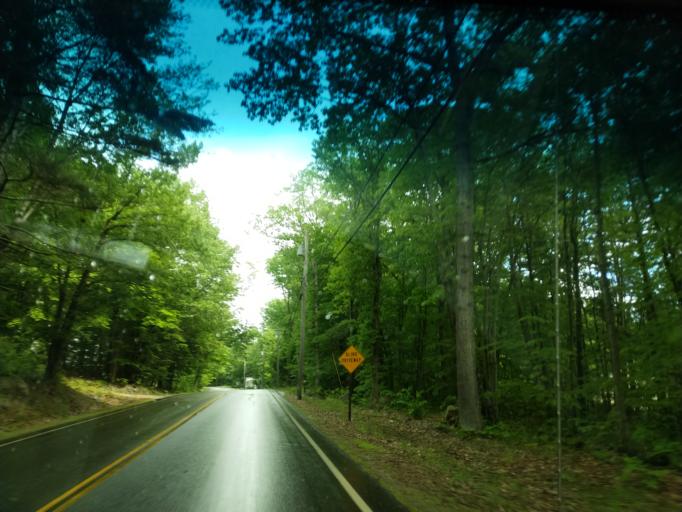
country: US
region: Maine
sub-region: Cumberland County
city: North Windham
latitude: 43.7962
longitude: -70.3645
